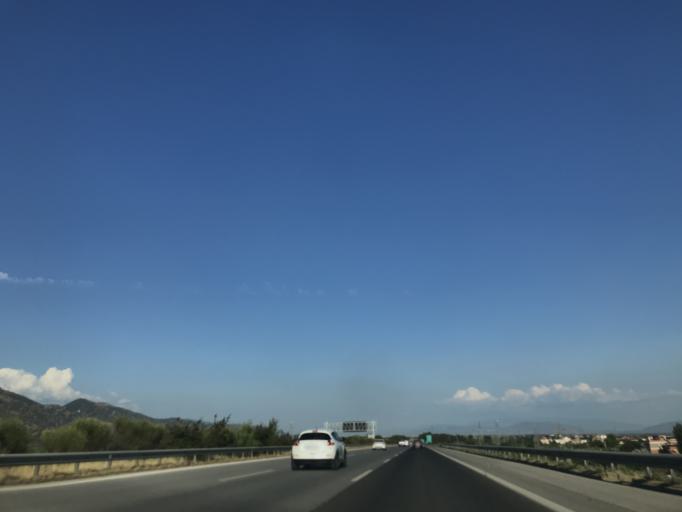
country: TR
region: Aydin
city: Germencik
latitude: 37.8801
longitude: 27.5947
